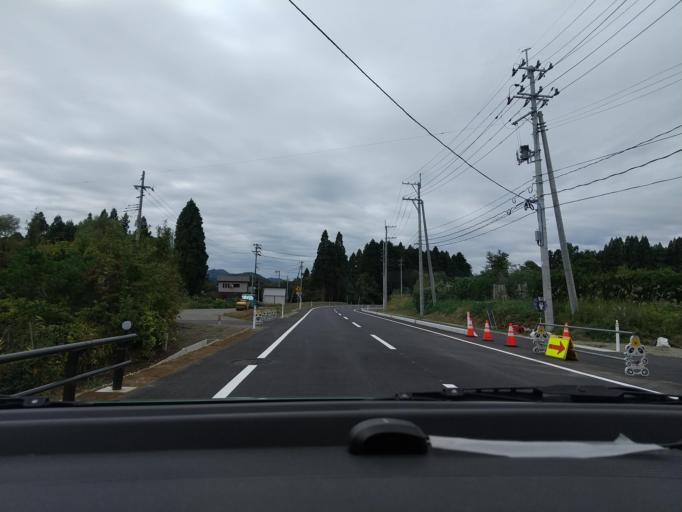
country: JP
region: Akita
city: Kakunodatemachi
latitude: 39.5819
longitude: 140.5764
